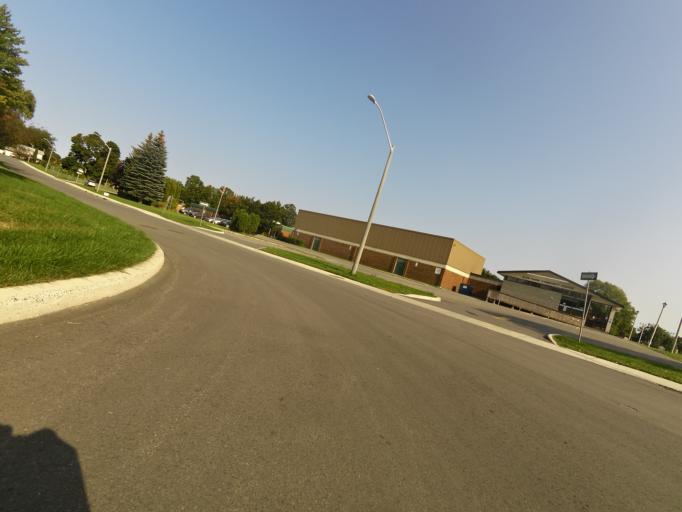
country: CA
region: Ontario
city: Bells Corners
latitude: 45.2964
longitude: -75.8858
